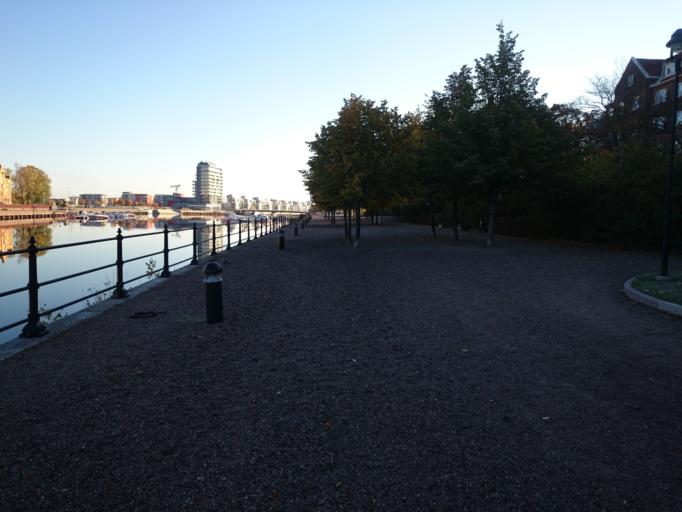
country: SE
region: Gaevleborg
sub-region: Gavle Kommun
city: Gavle
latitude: 60.6758
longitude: 17.1563
